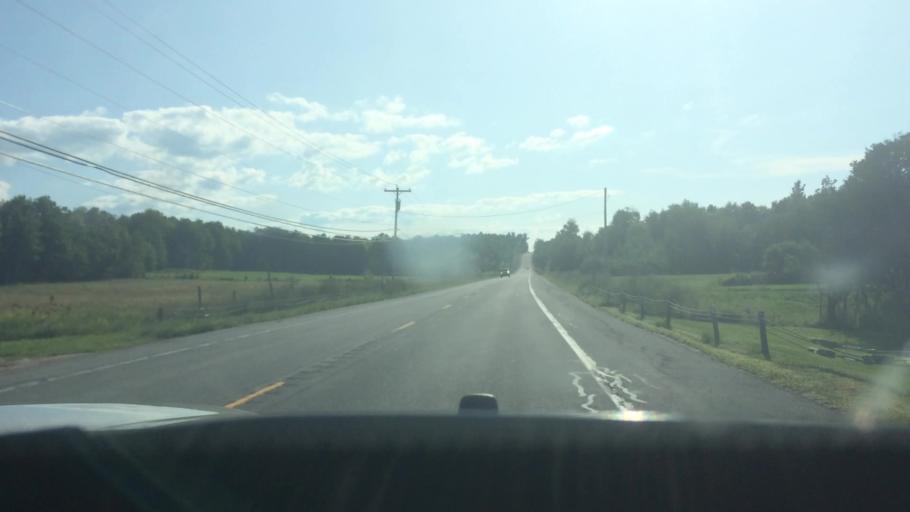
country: US
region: New York
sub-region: Franklin County
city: Malone
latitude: 44.8229
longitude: -74.3534
